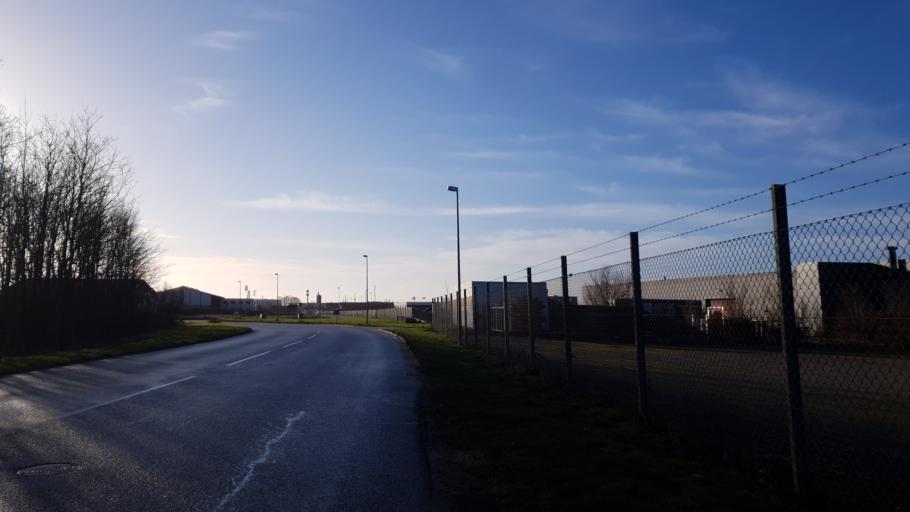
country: DK
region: Central Jutland
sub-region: Hedensted Kommune
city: Hedensted
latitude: 55.7993
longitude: 9.6761
